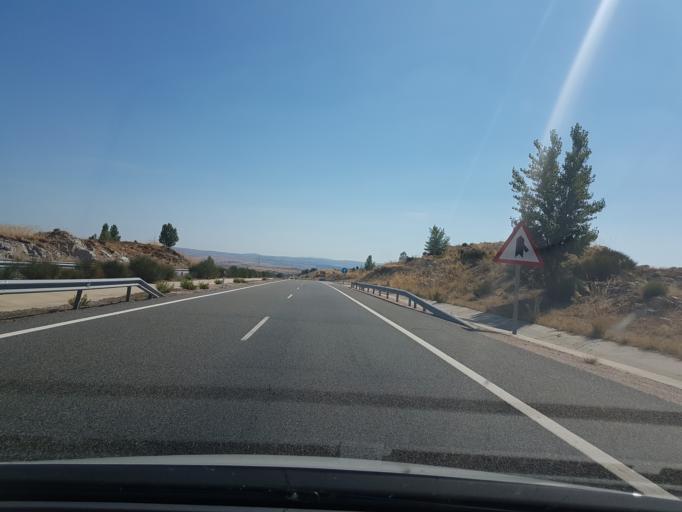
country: ES
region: Castille and Leon
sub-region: Provincia de Avila
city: Martiherrero
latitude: 40.6956
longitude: -4.7401
